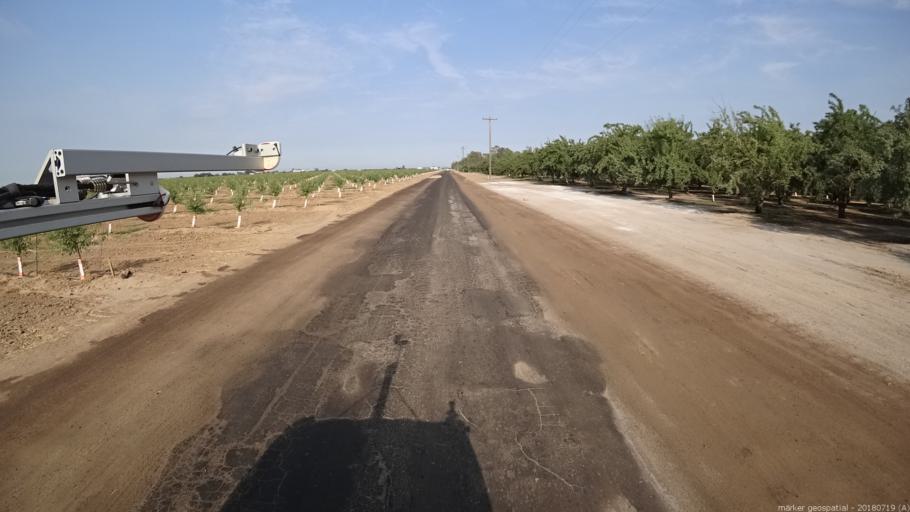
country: US
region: California
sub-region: Madera County
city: Fairmead
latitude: 37.0619
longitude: -120.1733
